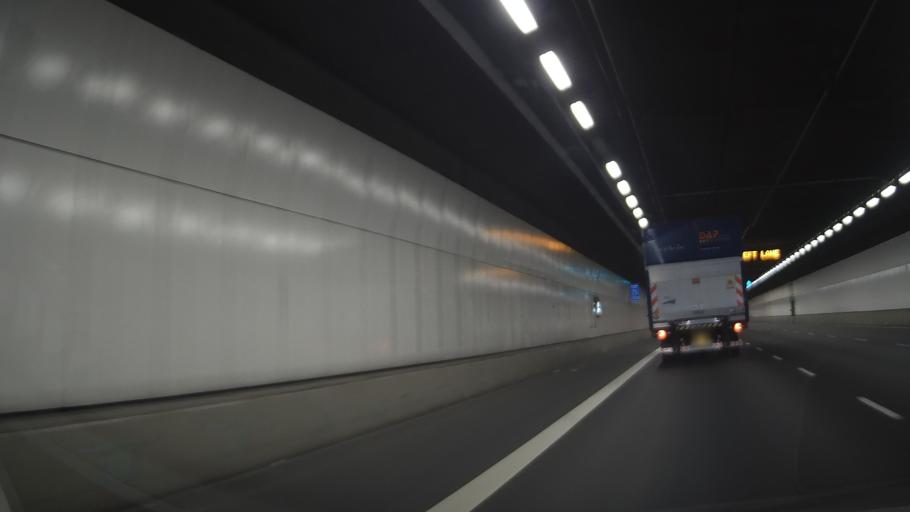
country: SG
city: Singapore
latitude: 1.3184
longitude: 103.8702
